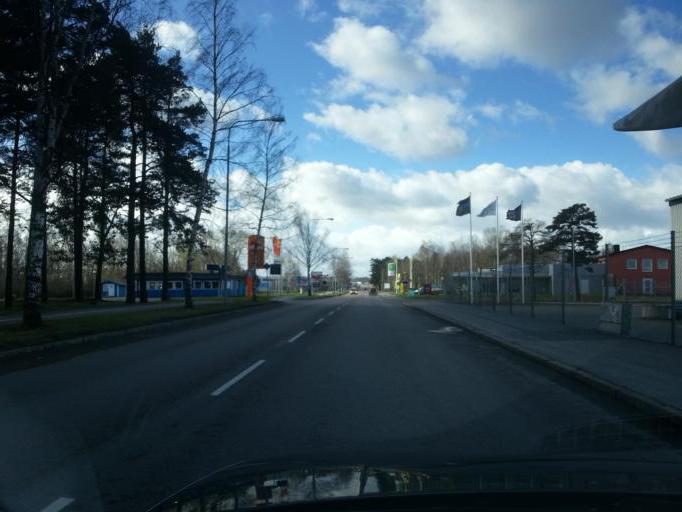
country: SE
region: Joenkoeping
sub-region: Jonkopings Kommun
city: Jonkoping
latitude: 57.7704
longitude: 14.1735
